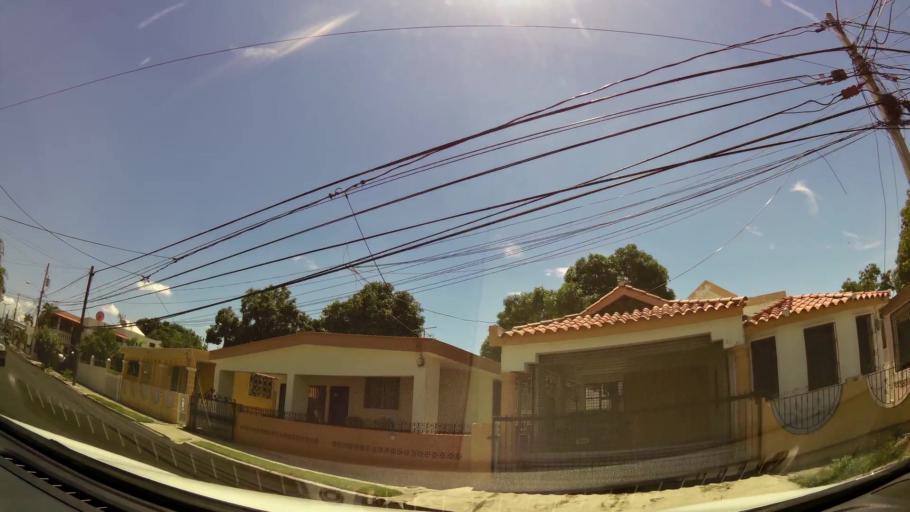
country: DO
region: Santiago
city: Santiago de los Caballeros
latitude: 19.4449
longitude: -70.6993
